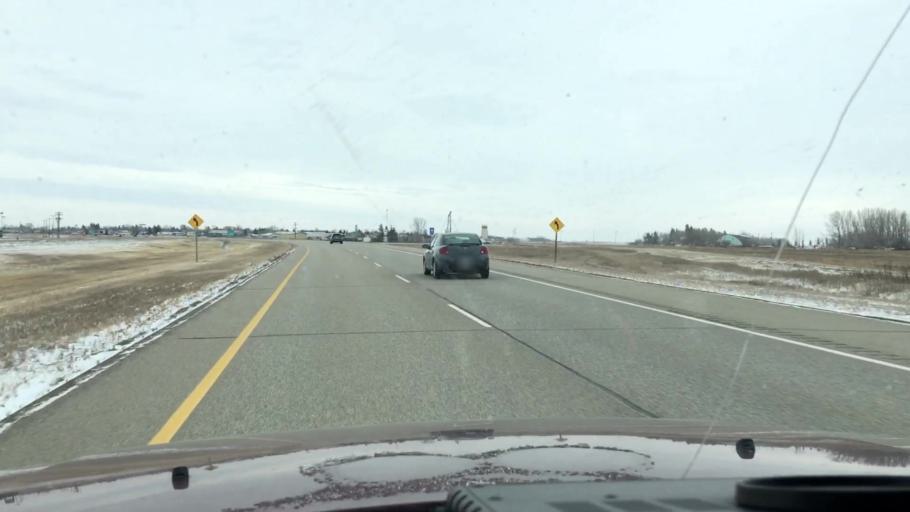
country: CA
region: Saskatchewan
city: Watrous
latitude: 51.2756
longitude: -106.0086
